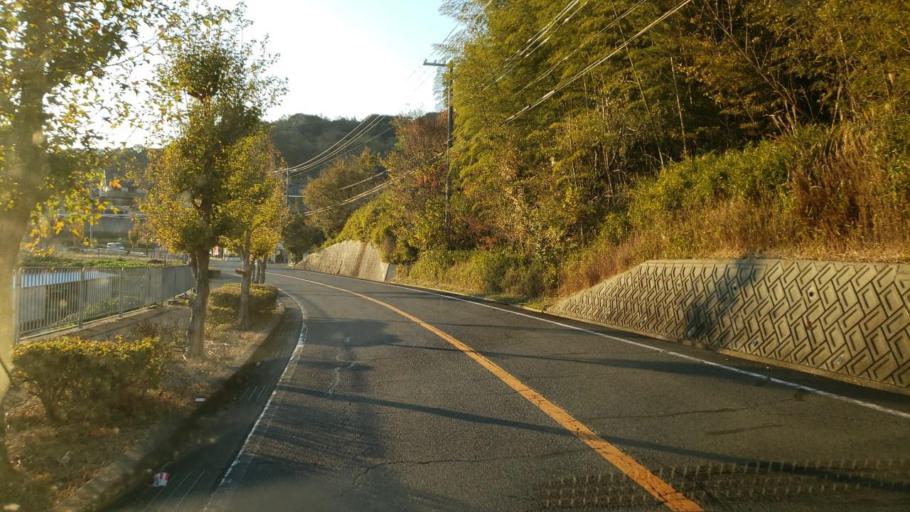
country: JP
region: Hyogo
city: Sumoto
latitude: 34.4432
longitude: 134.9009
